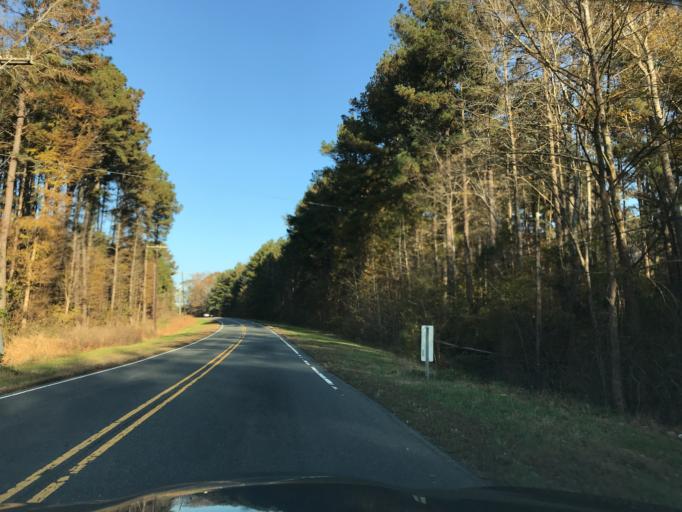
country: US
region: North Carolina
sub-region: Granville County
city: Butner
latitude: 36.0853
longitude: -78.7502
